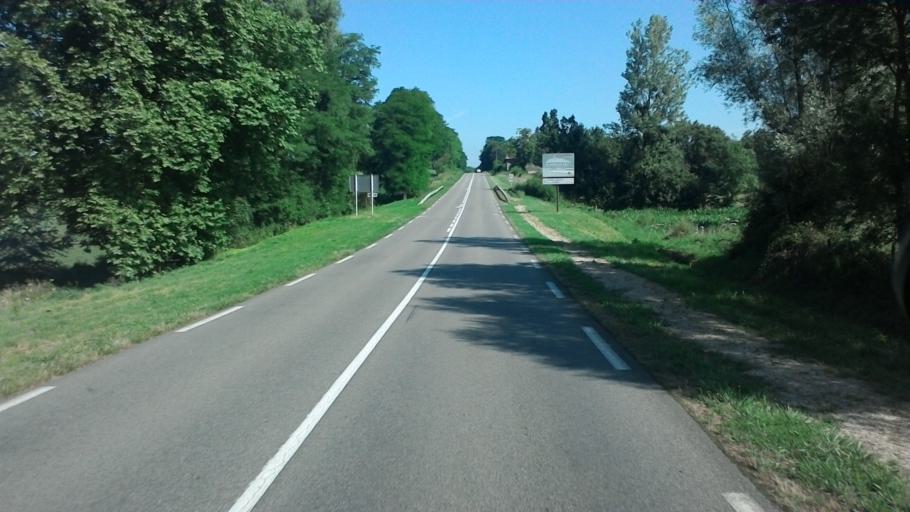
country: FR
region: Rhone-Alpes
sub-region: Departement de l'Ain
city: Saint-Trivier-de-Courtes
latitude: 46.4270
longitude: 5.0977
